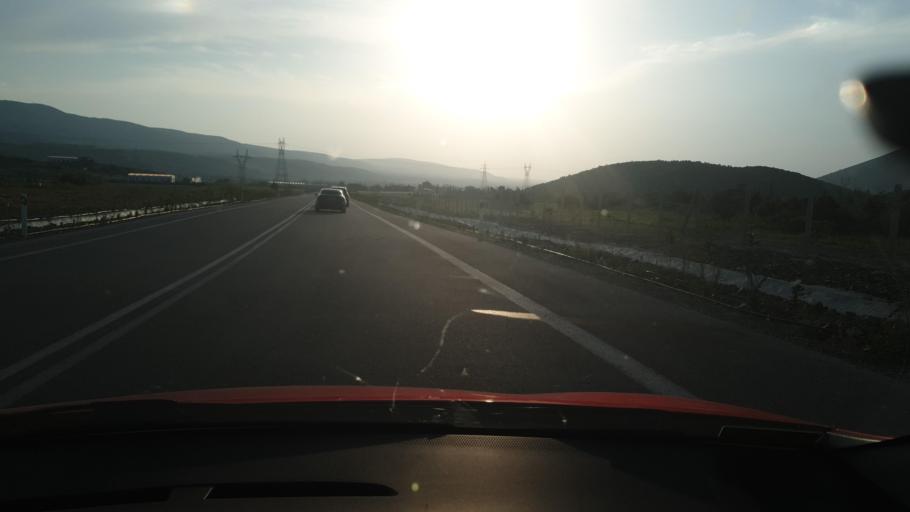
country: GR
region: Central Macedonia
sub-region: Nomos Chalkidikis
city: Galatista
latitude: 40.4662
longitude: 23.2082
